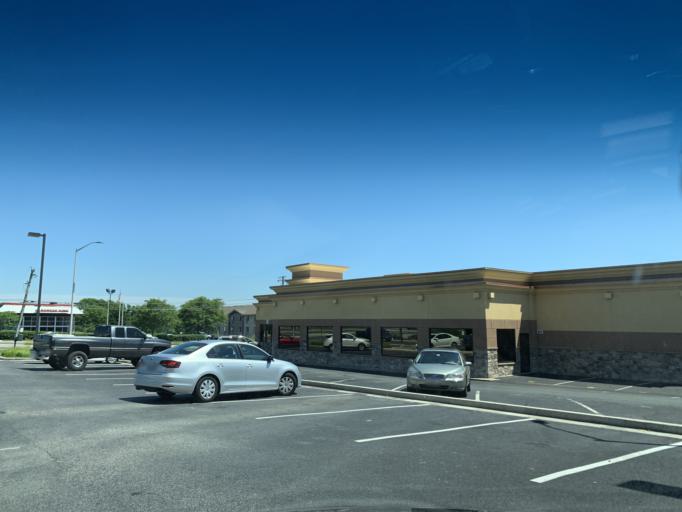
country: US
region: Maryland
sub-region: Harford County
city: Aberdeen
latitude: 39.5224
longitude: -76.1854
